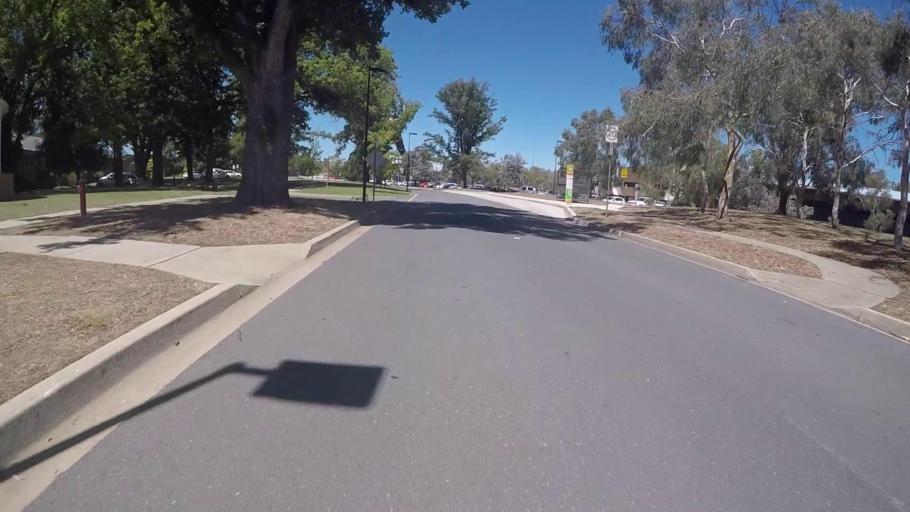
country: AU
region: Australian Capital Territory
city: Canberra
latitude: -35.2914
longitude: 149.1188
